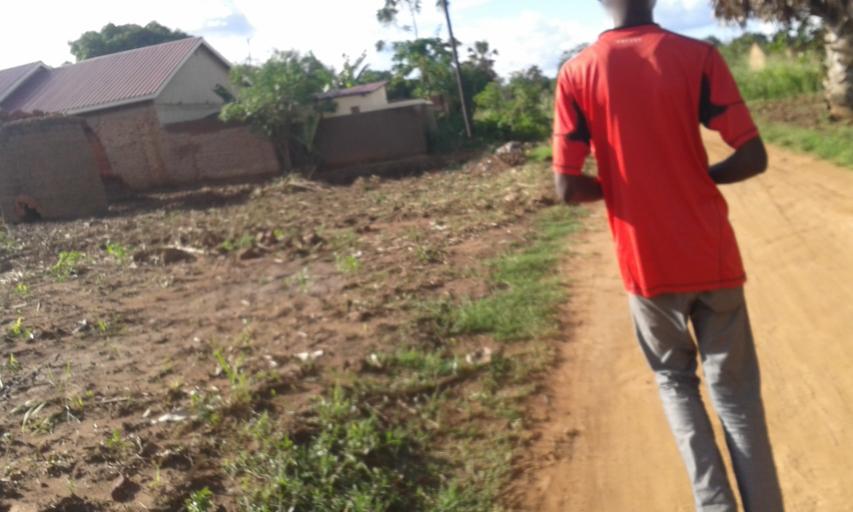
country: UG
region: Northern Region
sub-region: Gulu District
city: Gulu
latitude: 2.8024
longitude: 32.3059
